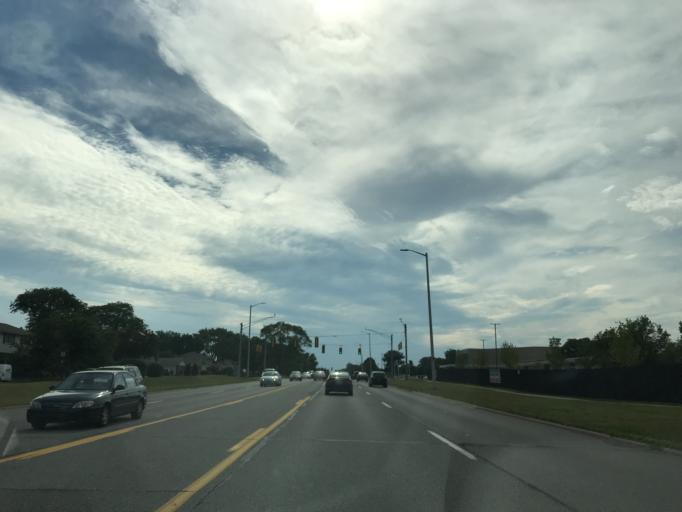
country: US
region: Michigan
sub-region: Wayne County
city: Livonia
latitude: 42.4116
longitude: -83.3792
